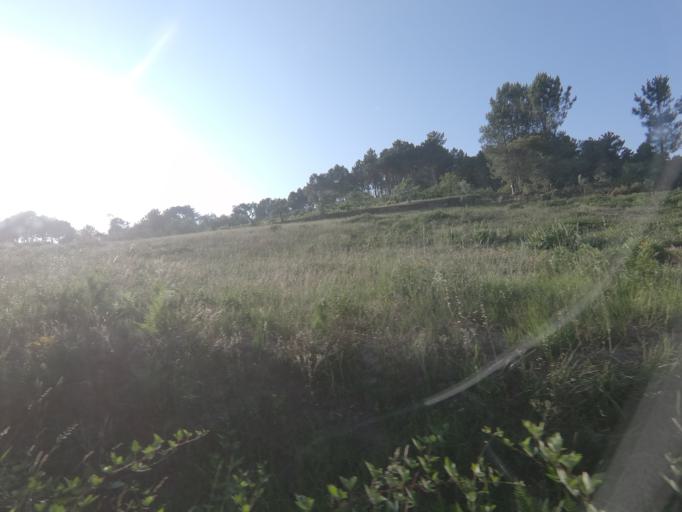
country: PT
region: Vila Real
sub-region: Vila Real
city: Vila Real
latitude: 41.2752
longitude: -7.6707
